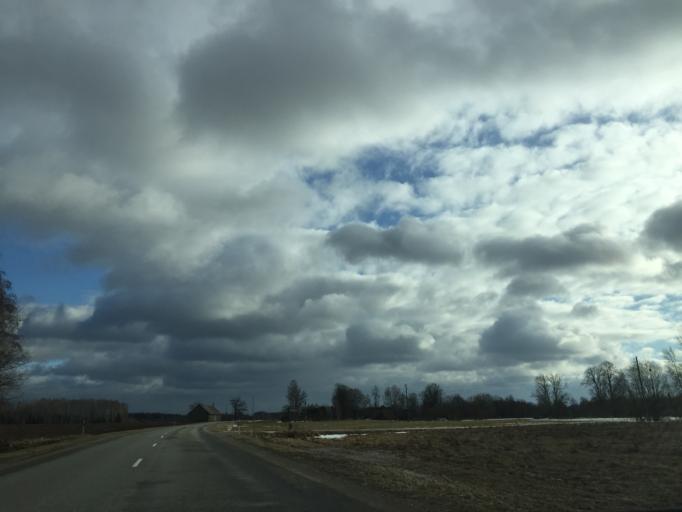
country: LV
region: Aloja
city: Staicele
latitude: 57.8741
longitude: 24.6769
